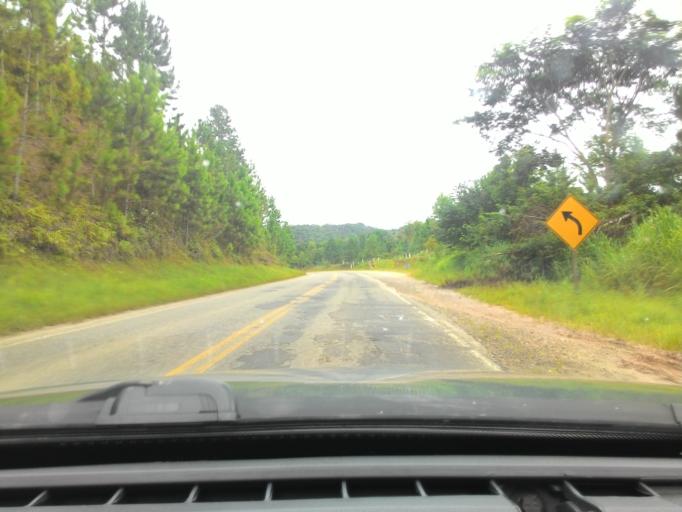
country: BR
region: Sao Paulo
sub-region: Pariquera-Acu
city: Pariquera Acu
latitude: -24.7299
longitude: -47.8477
